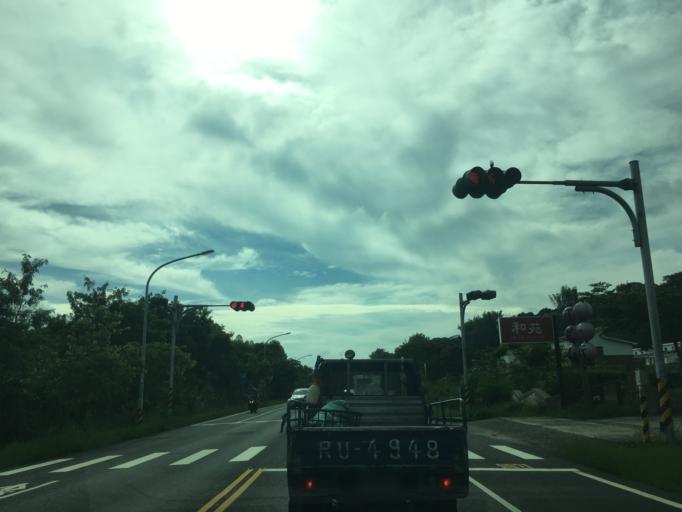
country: TW
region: Taiwan
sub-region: Chiayi
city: Jiayi Shi
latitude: 23.4510
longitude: 120.5687
